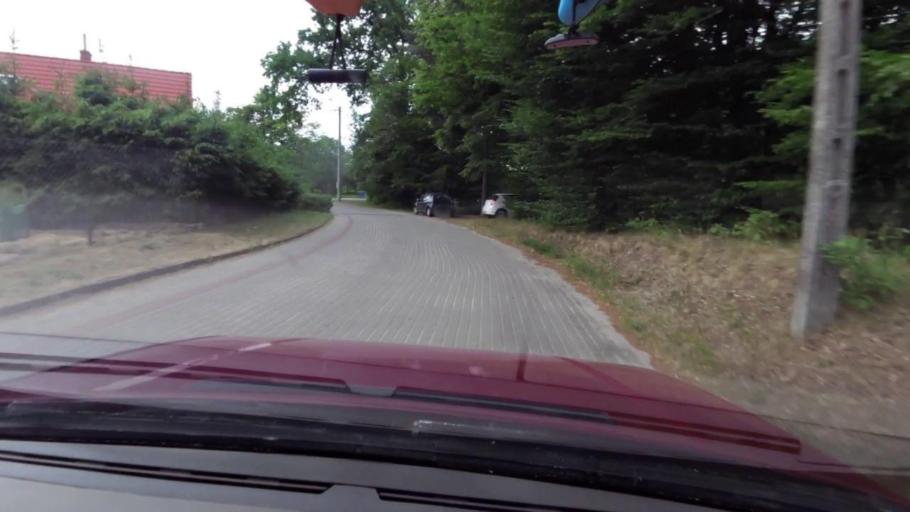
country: PL
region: Pomeranian Voivodeship
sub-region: Powiat slupski
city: Kepice
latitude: 54.2447
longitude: 16.8945
